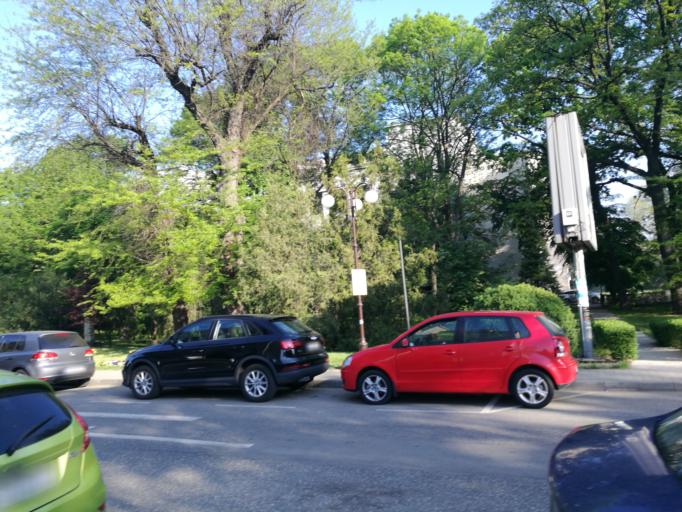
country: RO
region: Bucuresti
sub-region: Municipiul Bucuresti
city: Bucuresti
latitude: 44.4717
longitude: 26.0711
